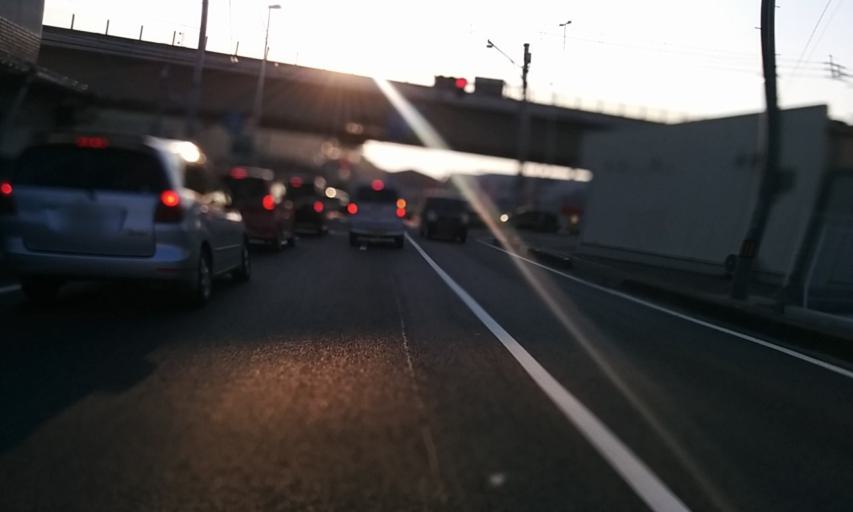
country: JP
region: Ehime
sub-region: Shikoku-chuo Shi
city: Matsuyama
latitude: 33.7819
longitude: 132.7881
